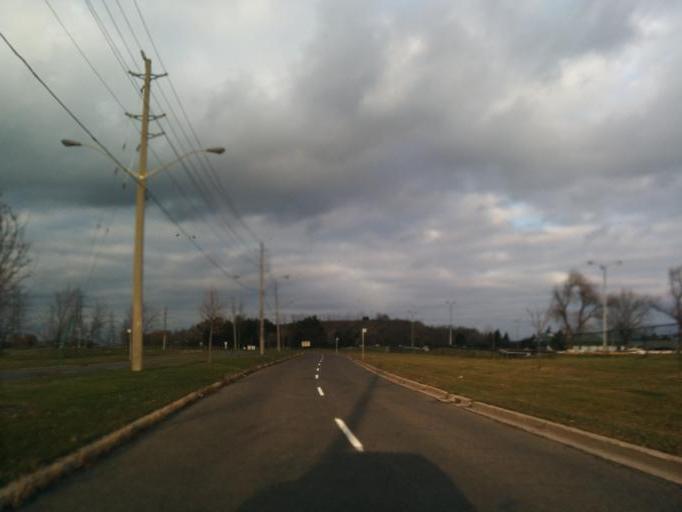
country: CA
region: Ontario
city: Etobicoke
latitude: 43.6505
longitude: -79.5952
